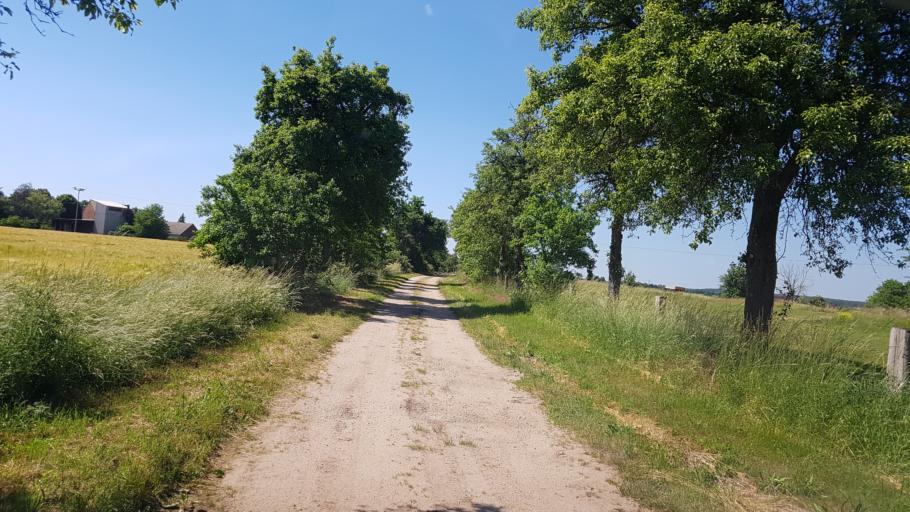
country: DE
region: Brandenburg
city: Sonnewalde
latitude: 51.6924
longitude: 13.6757
